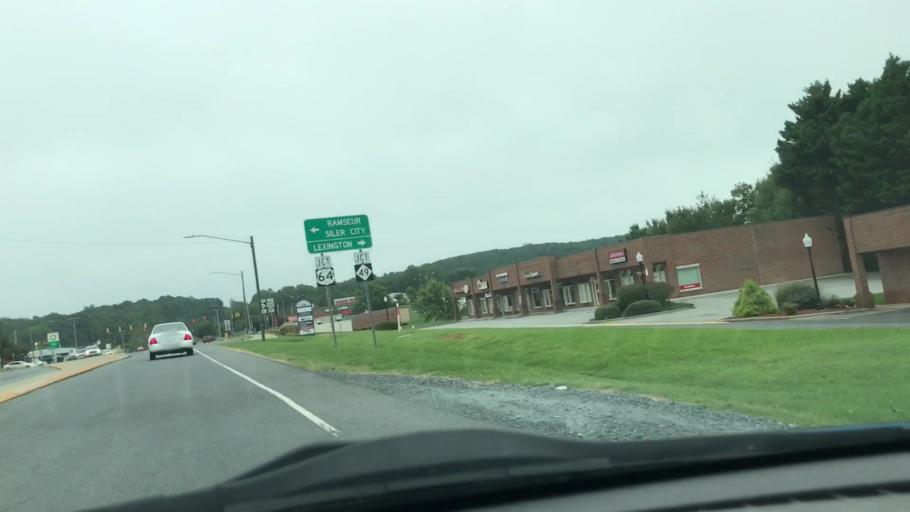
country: US
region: North Carolina
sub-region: Randolph County
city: Asheboro
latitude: 35.6995
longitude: -79.7899
